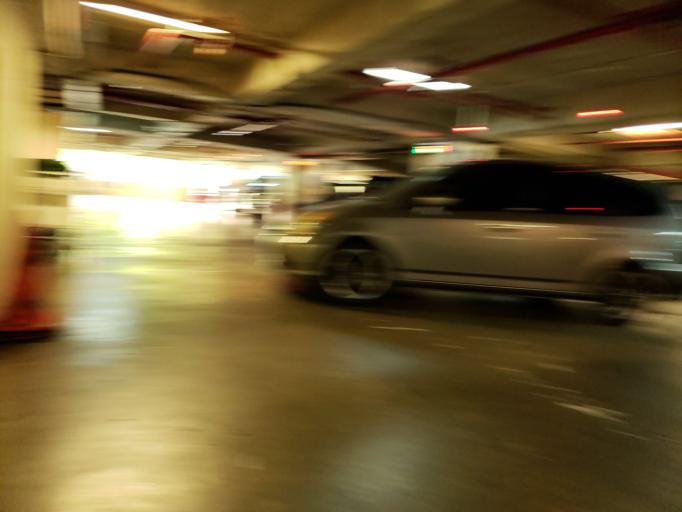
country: ID
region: Bali
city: Kelanabian
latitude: -8.7417
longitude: 115.1664
